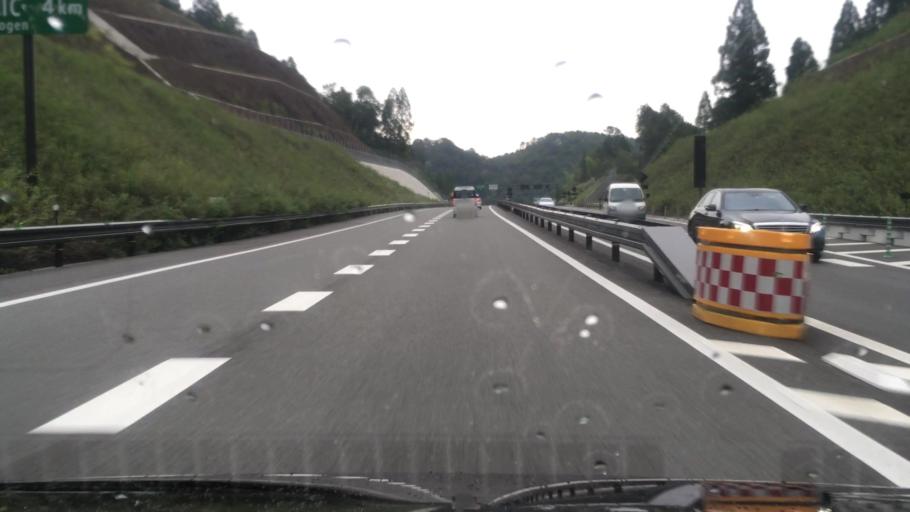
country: JP
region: Hyogo
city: Toyooka
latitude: 35.4284
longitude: 134.7670
